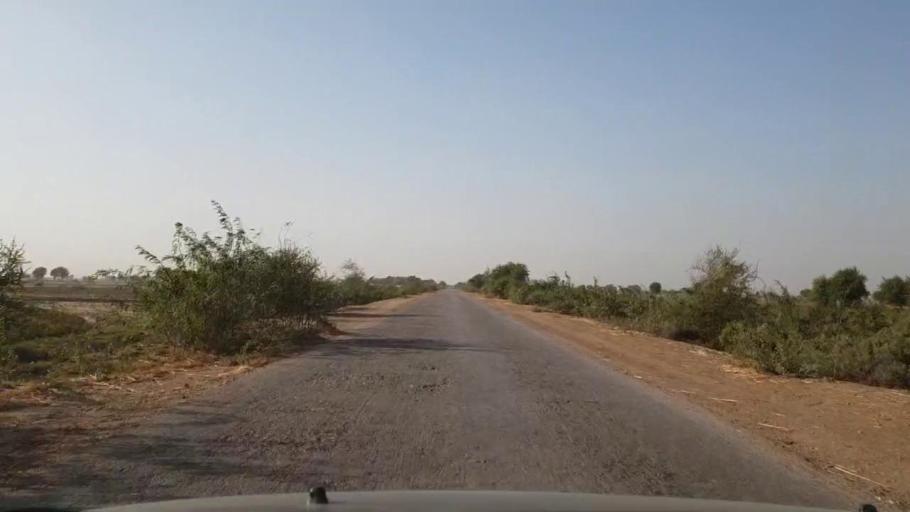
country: PK
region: Sindh
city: Tando Ghulam Ali
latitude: 25.1823
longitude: 68.8202
